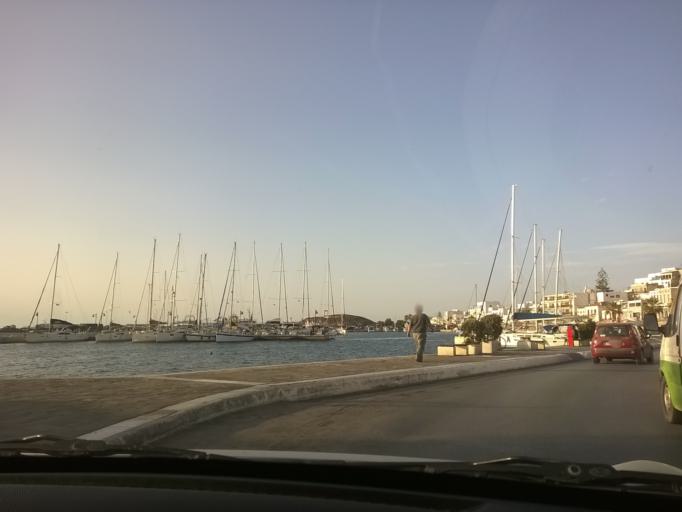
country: GR
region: South Aegean
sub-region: Nomos Kykladon
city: Naxos
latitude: 37.1037
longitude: 25.3752
